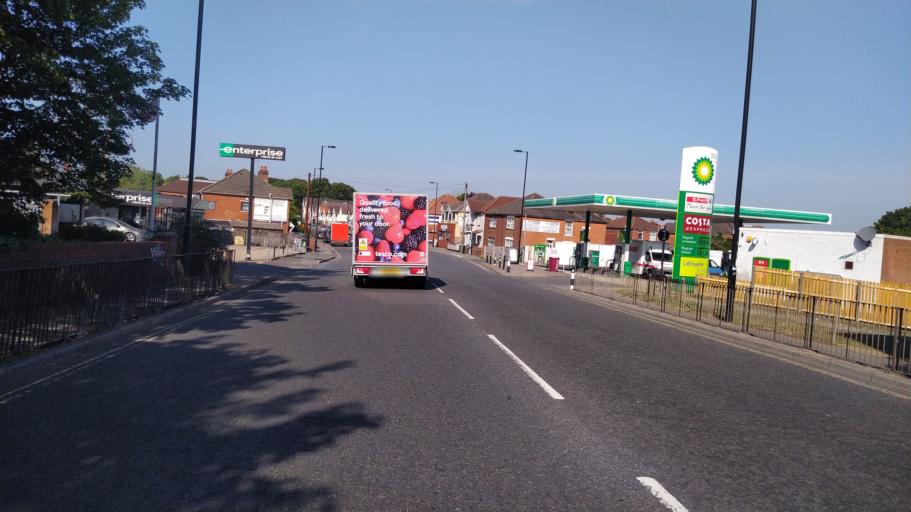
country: GB
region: England
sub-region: Southampton
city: Southampton
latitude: 50.9179
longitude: -1.3784
